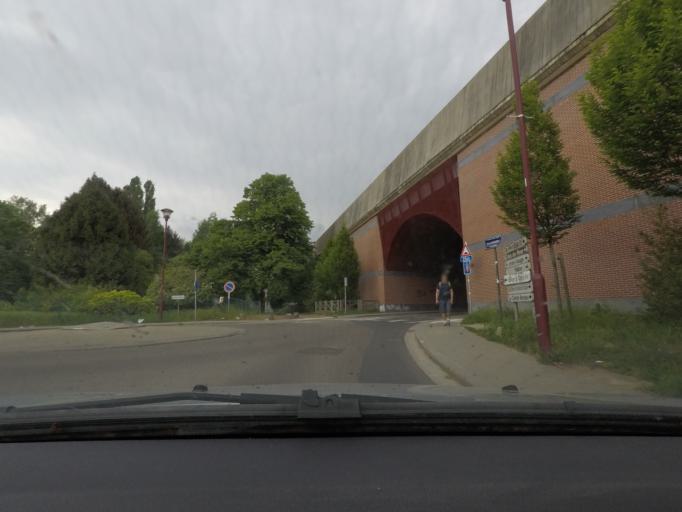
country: BE
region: Wallonia
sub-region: Province du Brabant Wallon
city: Ottignies
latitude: 50.6666
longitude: 4.5711
